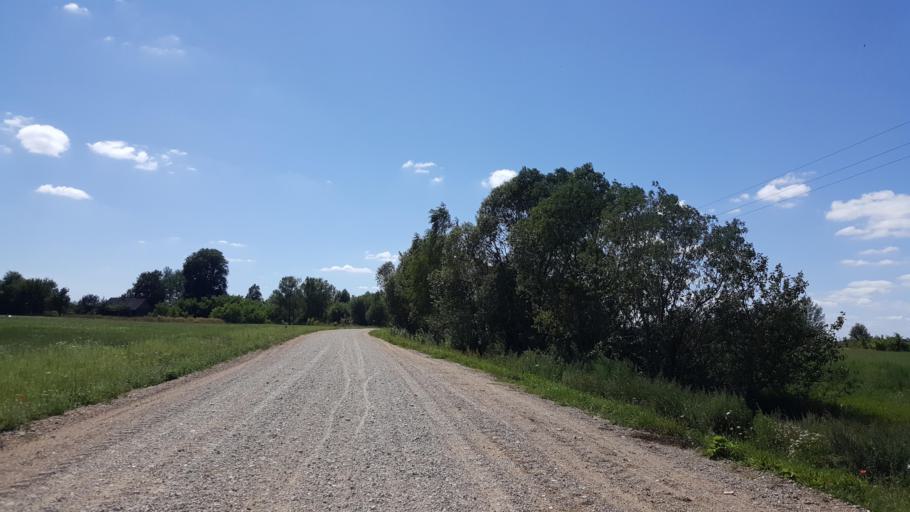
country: BY
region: Brest
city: Horad Kobryn
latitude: 52.3139
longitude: 24.3912
